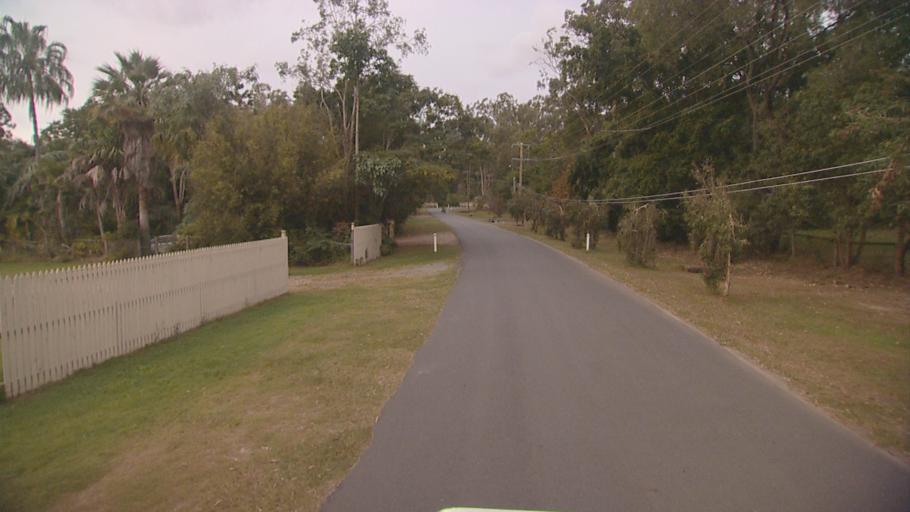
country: AU
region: Queensland
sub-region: Logan
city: Park Ridge South
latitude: -27.6818
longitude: 153.0154
